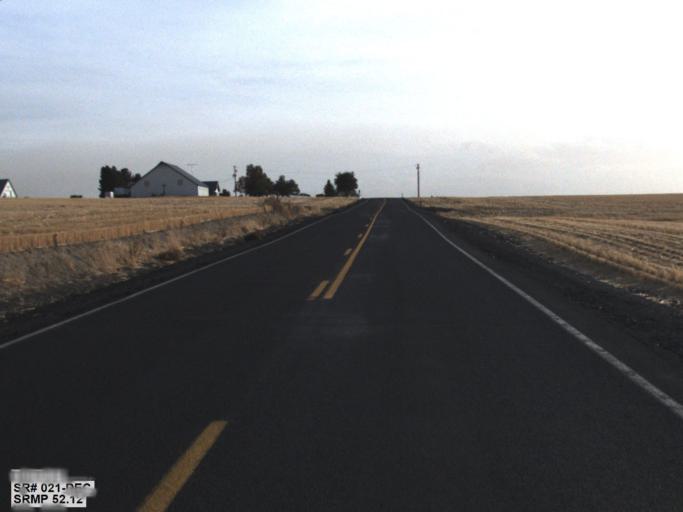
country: US
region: Washington
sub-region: Adams County
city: Ritzville
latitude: 47.2839
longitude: -118.6905
